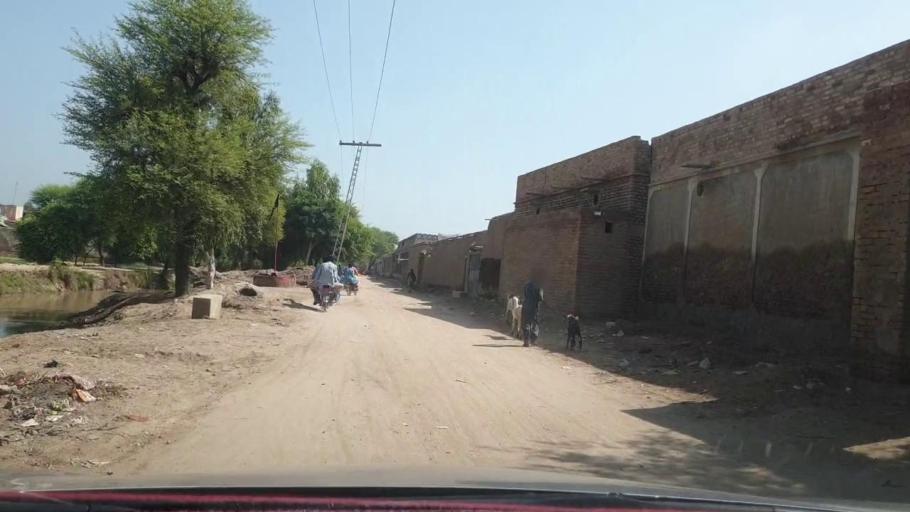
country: PK
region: Sindh
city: Warah
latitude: 27.4821
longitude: 67.8297
